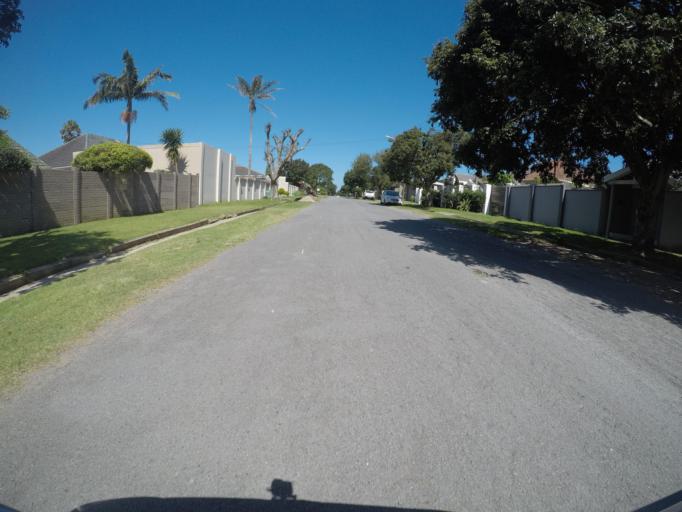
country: ZA
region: Eastern Cape
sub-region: Buffalo City Metropolitan Municipality
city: East London
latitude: -32.9867
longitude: 27.9340
